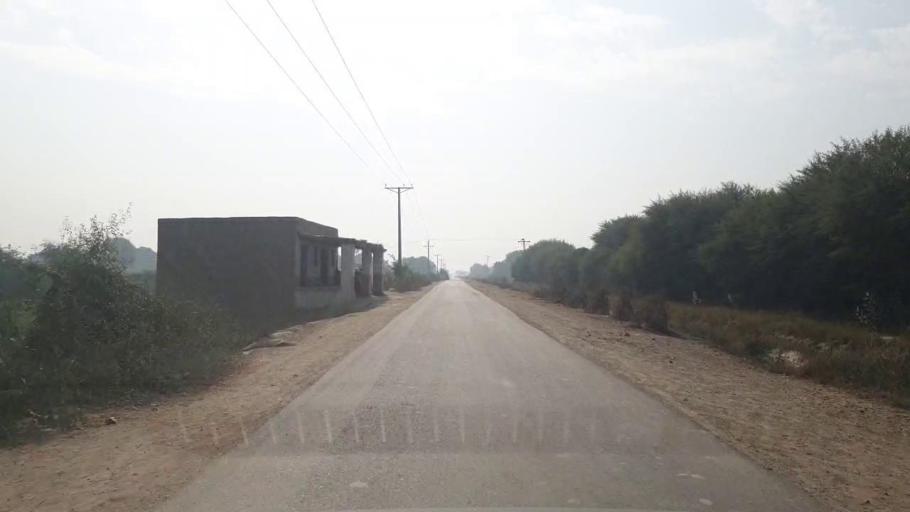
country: PK
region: Sindh
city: Hala
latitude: 25.7942
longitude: 68.4393
